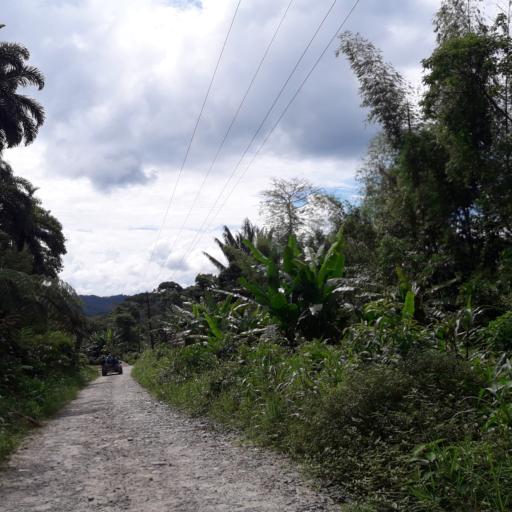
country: EC
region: Napo
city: Archidona
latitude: -0.9406
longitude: -77.8801
